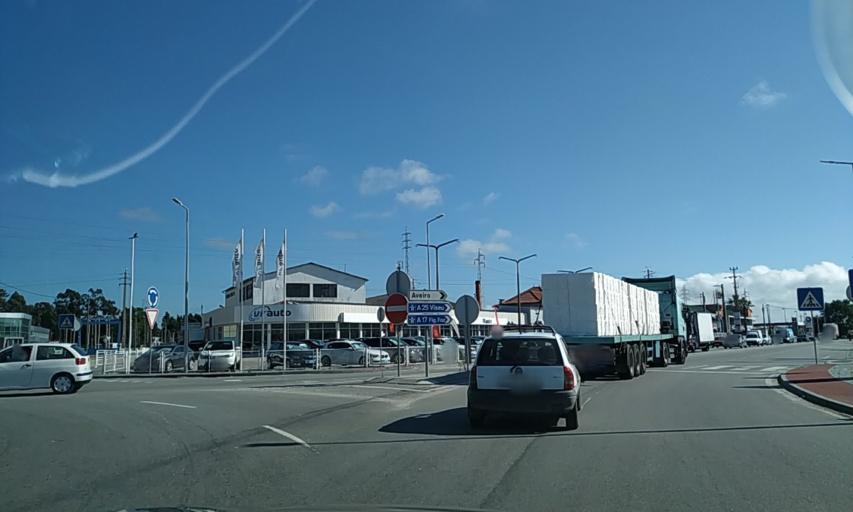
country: PT
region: Aveiro
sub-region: Aveiro
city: Aveiro
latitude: 40.6638
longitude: -8.6115
